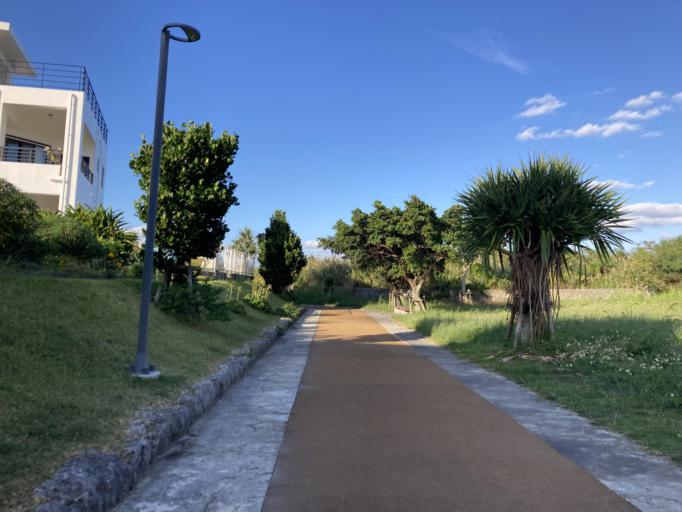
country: JP
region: Okinawa
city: Ginowan
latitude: 26.2560
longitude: 127.7776
